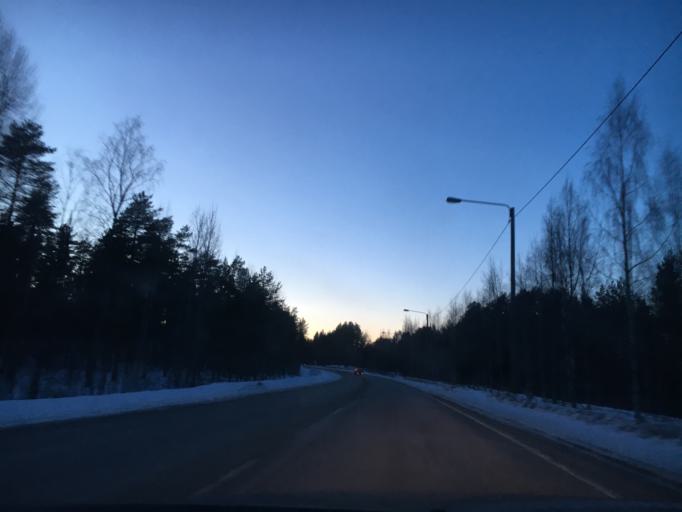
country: FI
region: Kainuu
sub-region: Kajaani
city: Kajaani
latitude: 64.2016
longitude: 27.7451
